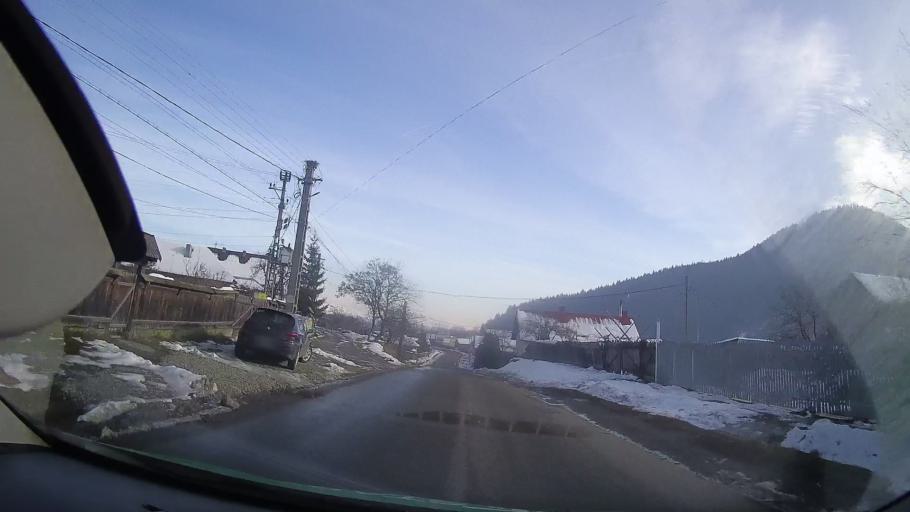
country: RO
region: Neamt
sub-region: Comuna Garcina
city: Garcina
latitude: 46.9759
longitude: 26.3521
